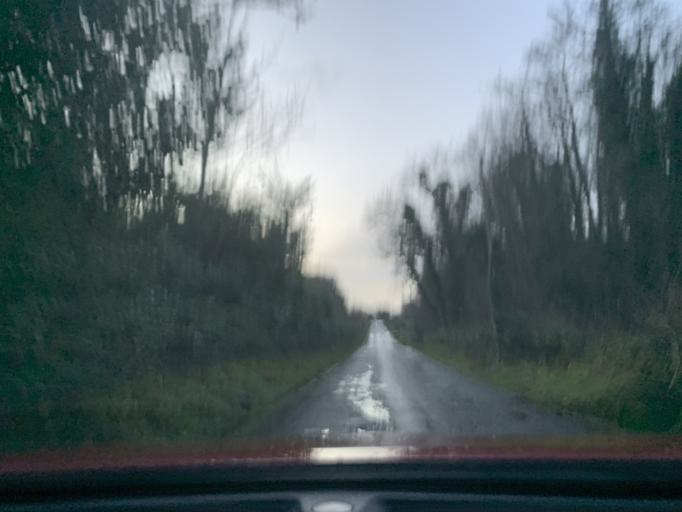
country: IE
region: Connaught
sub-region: Sligo
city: Ballymote
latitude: 54.1240
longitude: -8.5865
